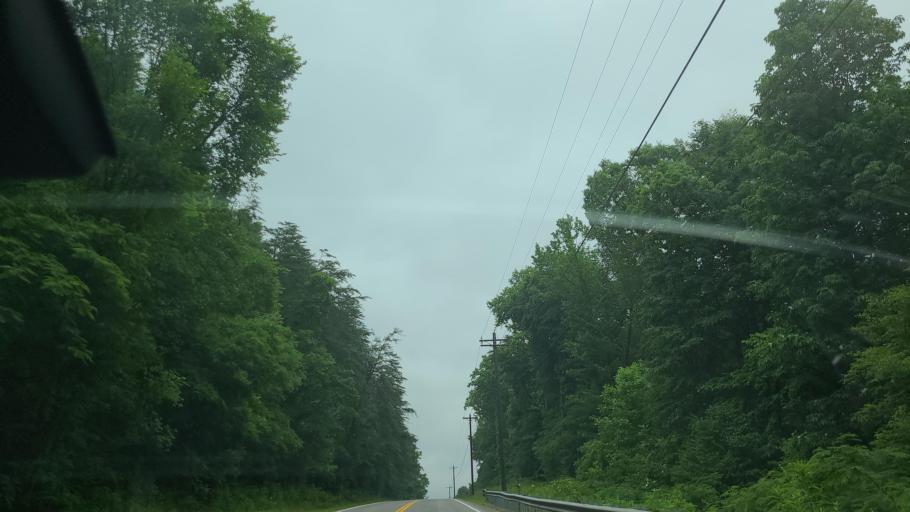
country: US
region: Tennessee
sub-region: Anderson County
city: Oak Ridge
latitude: 36.1005
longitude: -84.2508
